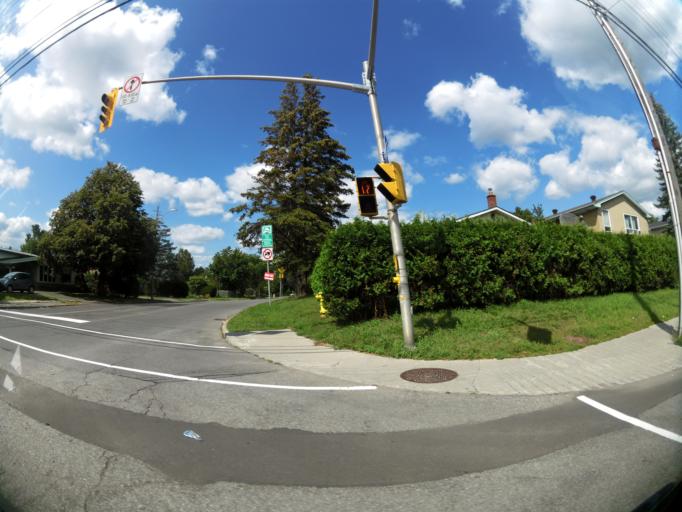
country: CA
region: Ontario
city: Ottawa
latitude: 45.3852
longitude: -75.6271
